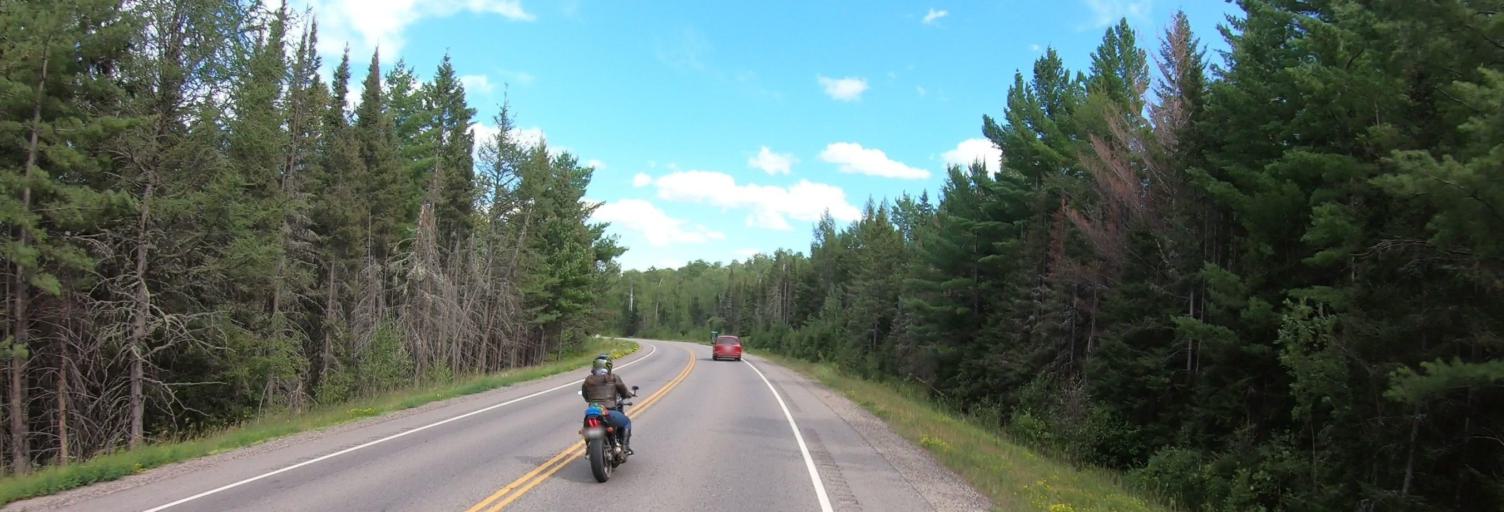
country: US
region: Minnesota
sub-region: Saint Louis County
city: Ely
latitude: 47.8801
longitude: -91.9789
